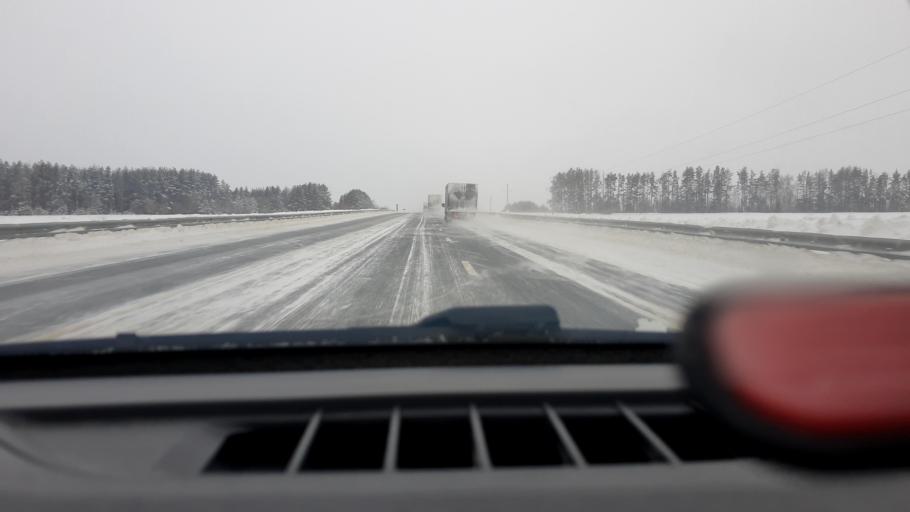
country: RU
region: Nizjnij Novgorod
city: Bol'shoye Murashkino
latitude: 55.8926
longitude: 44.7385
